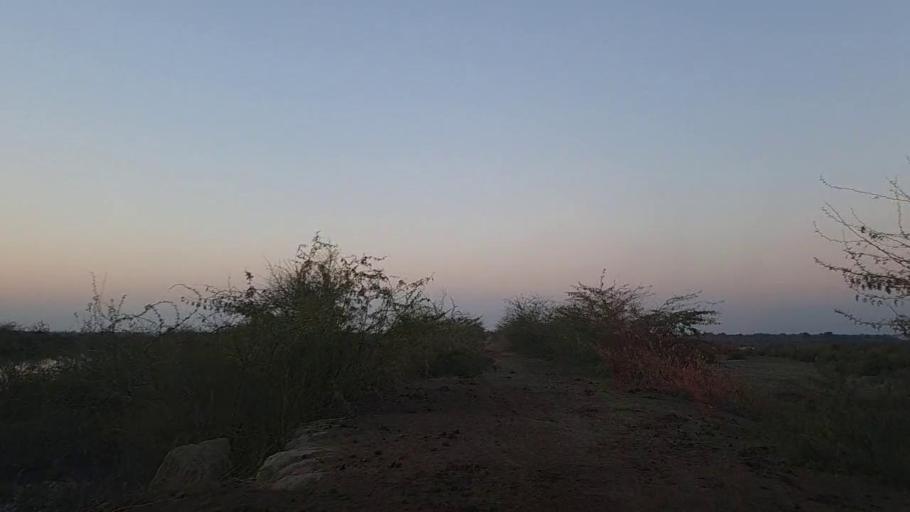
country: PK
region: Sindh
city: Tando Mittha Khan
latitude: 26.0754
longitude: 69.1542
